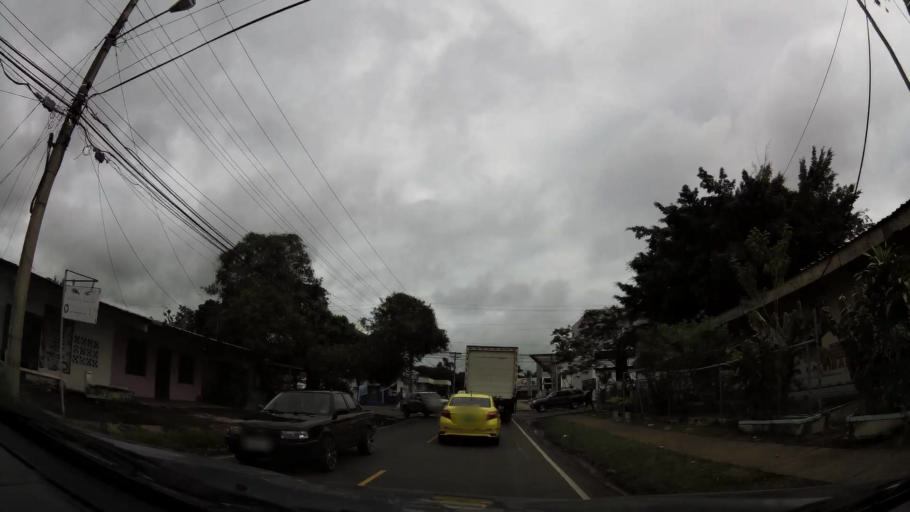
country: PA
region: Chiriqui
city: David
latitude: 8.4303
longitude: -82.4309
